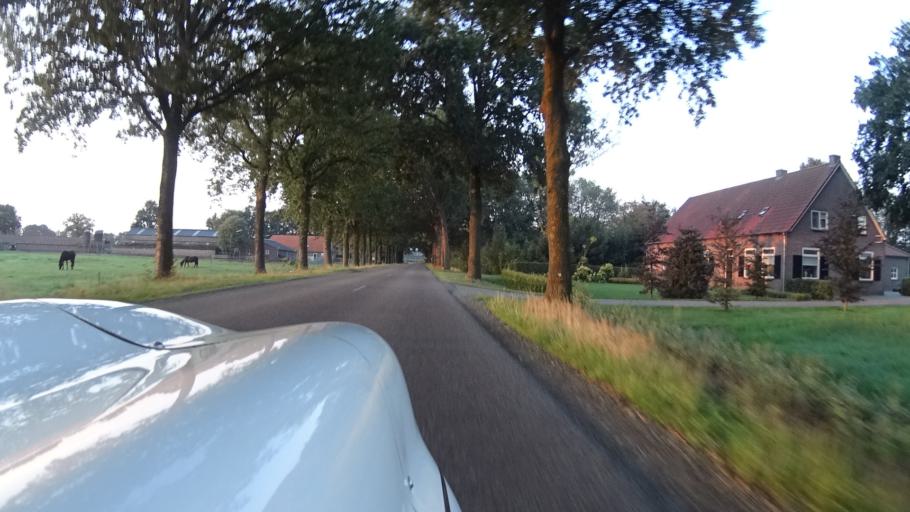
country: NL
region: North Brabant
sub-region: Gemeente Mill en Sint Hubert
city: Wilbertoord
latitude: 51.6064
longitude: 5.7838
